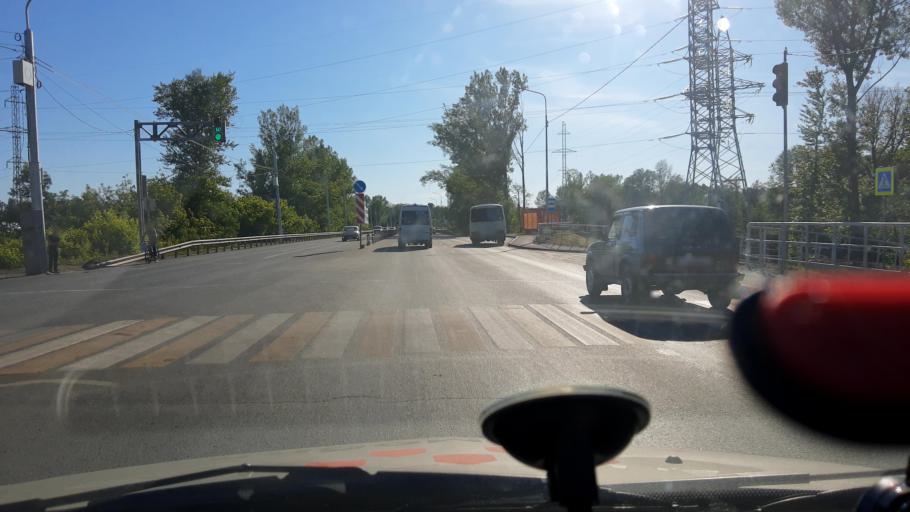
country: RU
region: Bashkortostan
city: Ufa
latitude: 54.7002
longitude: 55.9009
